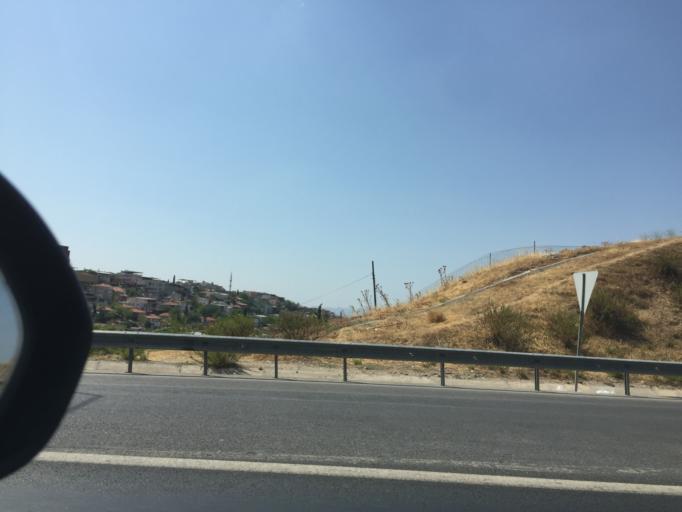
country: TR
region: Izmir
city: Karsiyaka
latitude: 38.4858
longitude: 27.1352
